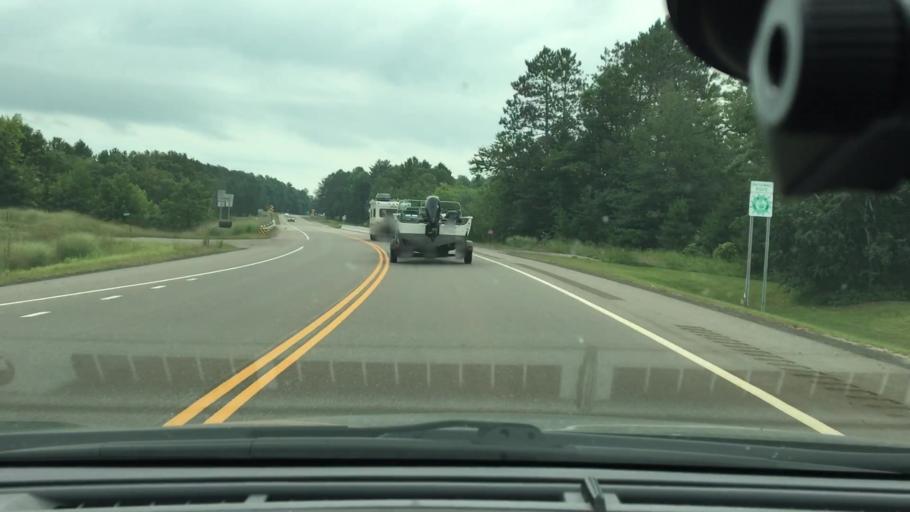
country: US
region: Minnesota
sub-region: Crow Wing County
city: Crosby
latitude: 46.5451
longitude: -93.9574
